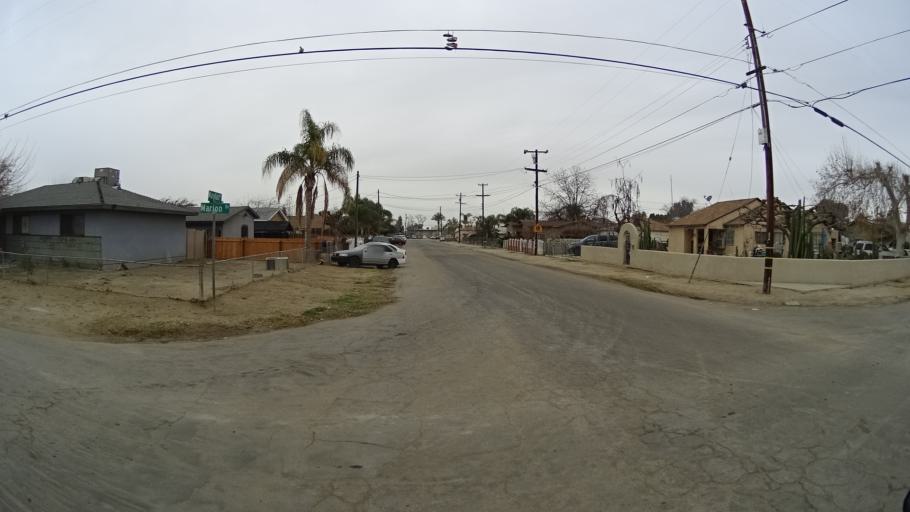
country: US
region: California
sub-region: Kern County
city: Lamont
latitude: 35.3416
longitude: -118.9297
